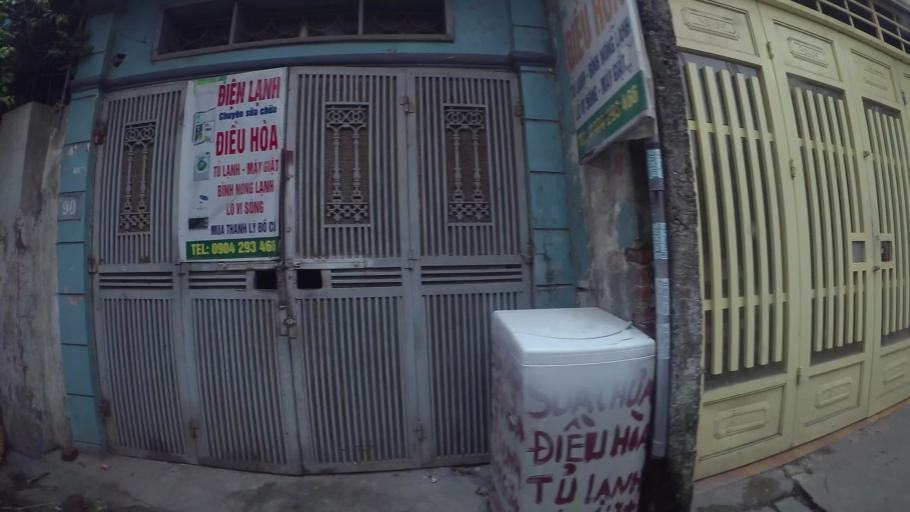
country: VN
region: Ha Noi
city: Van Dien
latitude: 20.9775
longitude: 105.8505
